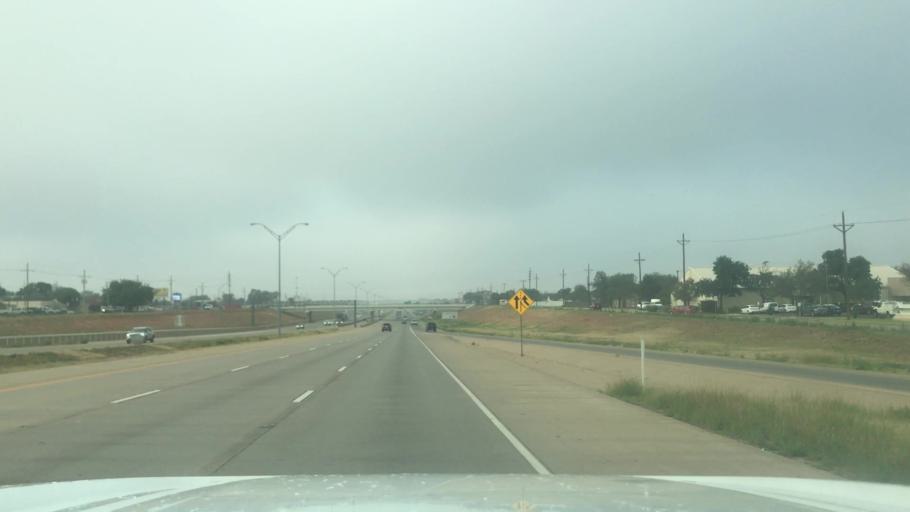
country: US
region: Texas
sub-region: Lubbock County
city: Lubbock
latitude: 33.5601
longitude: -101.8452
